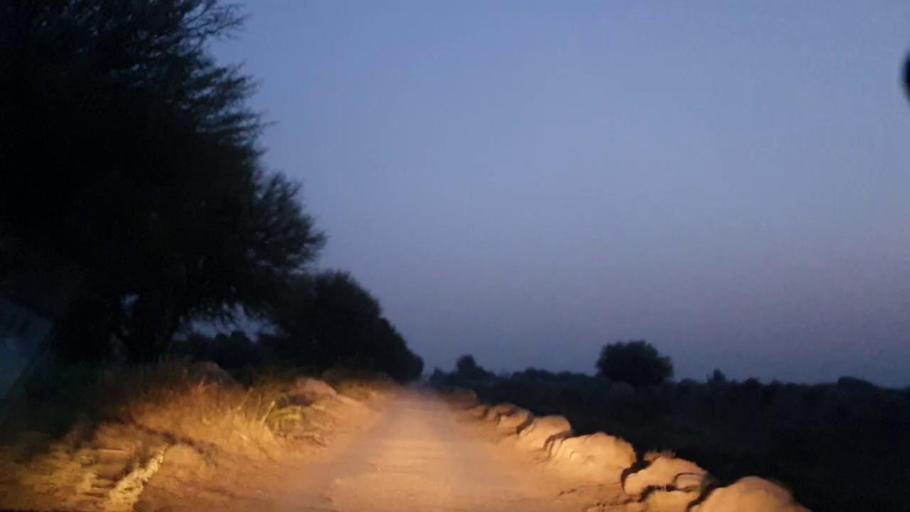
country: PK
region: Sindh
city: Tando Ghulam Ali
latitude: 25.0956
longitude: 68.9147
